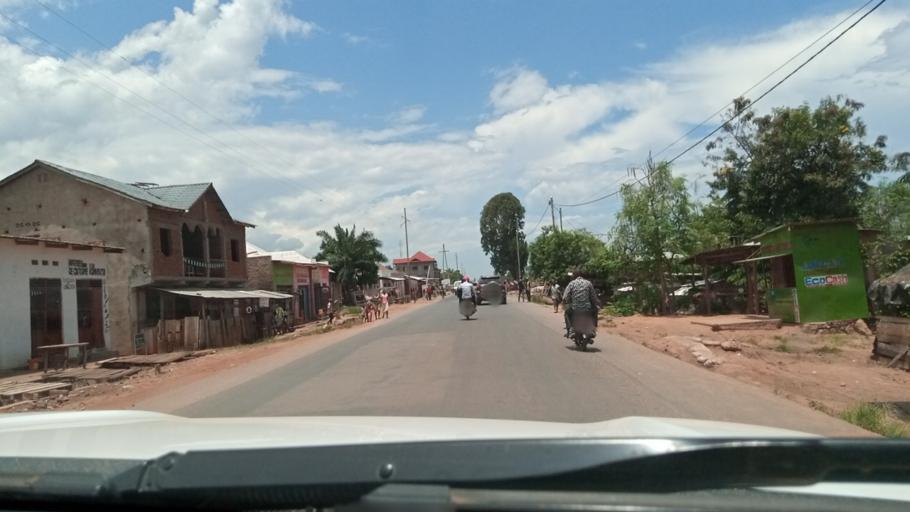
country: BI
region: Bujumbura Mairie
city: Bujumbura
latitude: -3.4613
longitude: 29.3506
